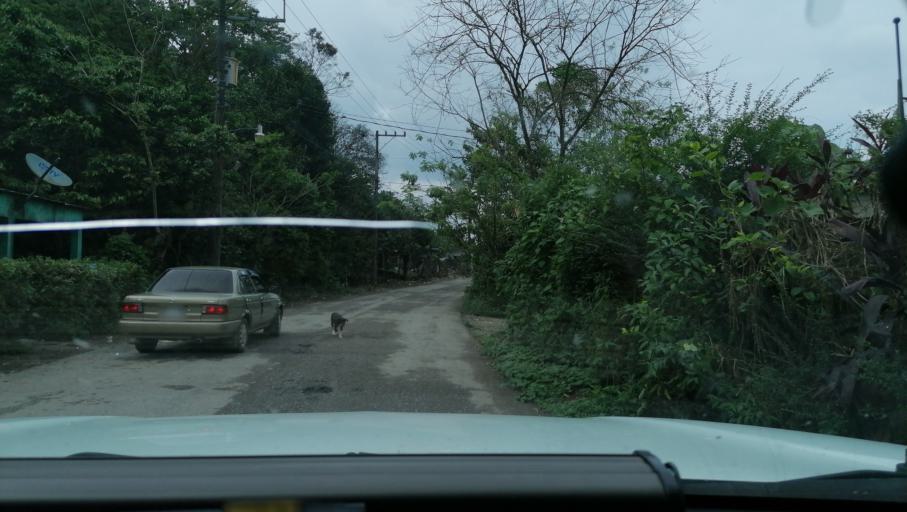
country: MX
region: Chiapas
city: Ixtacomitan
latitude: 17.3352
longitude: -93.1300
